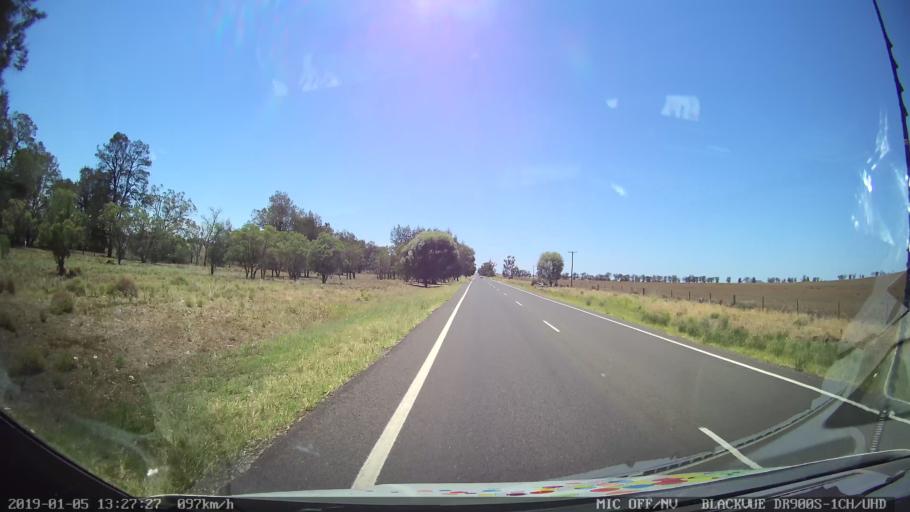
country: AU
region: New South Wales
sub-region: Gunnedah
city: Gunnedah
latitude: -31.0444
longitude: 150.0295
